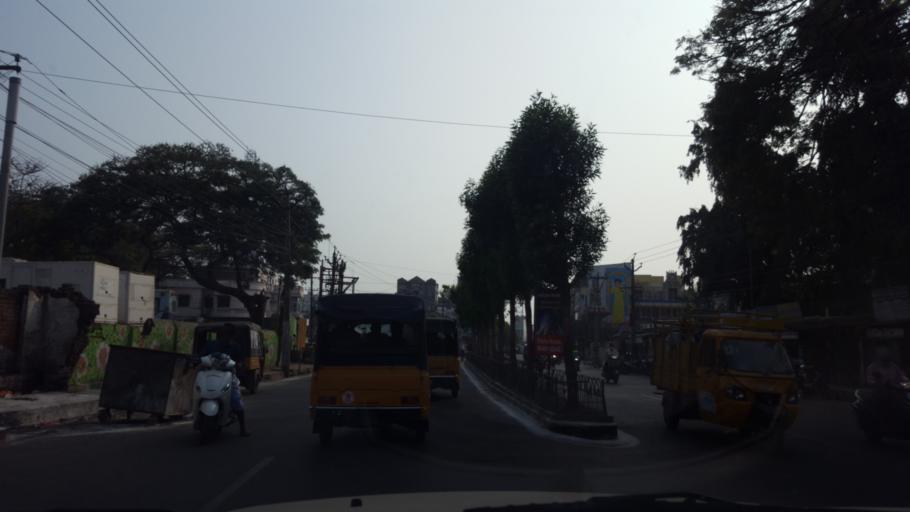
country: IN
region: Andhra Pradesh
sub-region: Srikakulam
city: Srikakulam
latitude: 18.2971
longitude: 83.8947
